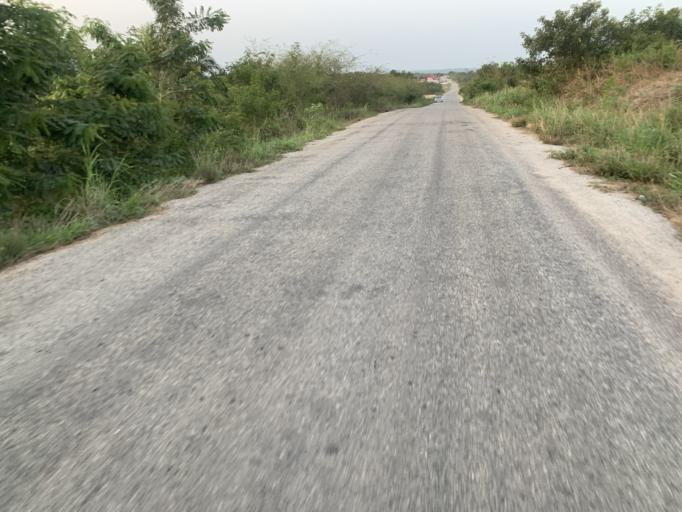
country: GH
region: Central
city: Winneba
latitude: 5.3719
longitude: -0.6153
